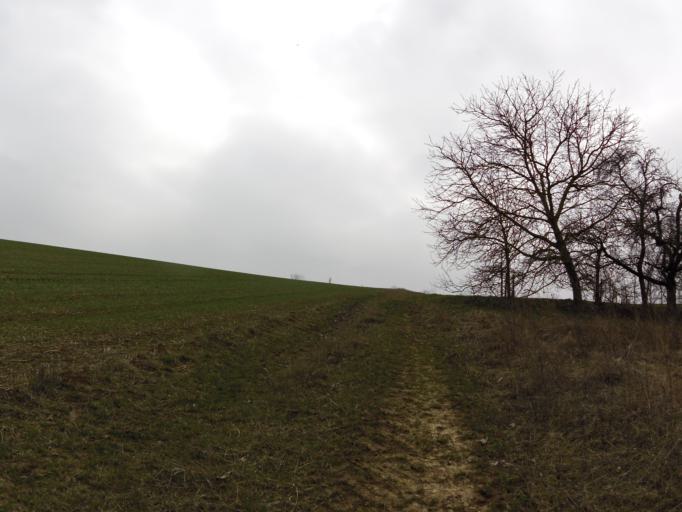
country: DE
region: Bavaria
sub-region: Regierungsbezirk Unterfranken
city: Estenfeld
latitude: 49.8194
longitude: 10.0174
